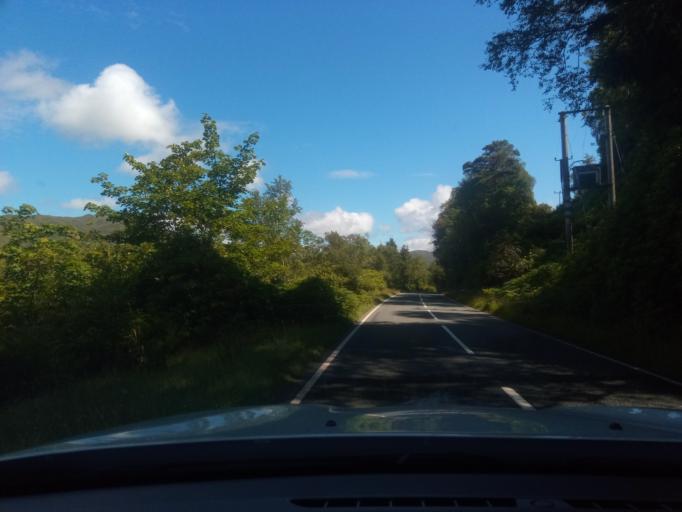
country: GB
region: Scotland
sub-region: Argyll and Bute
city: Isle Of Mull
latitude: 56.8701
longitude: -5.6758
